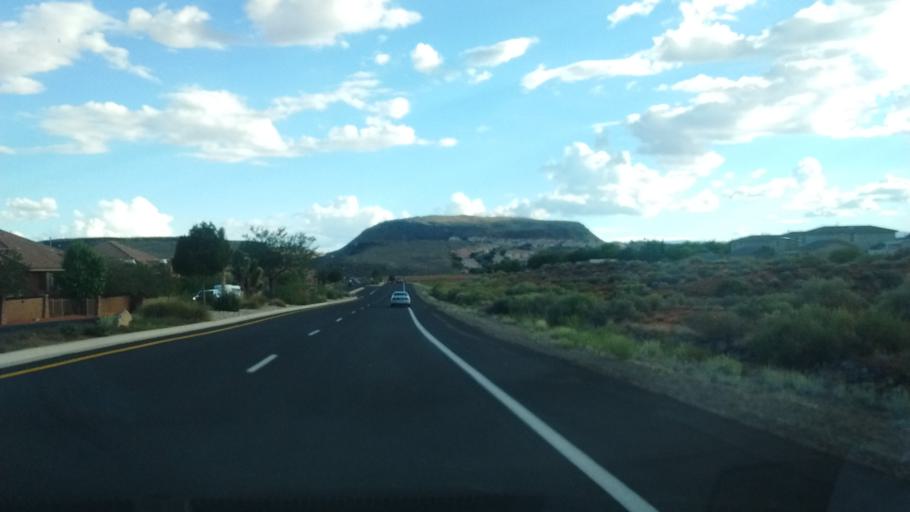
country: US
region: Utah
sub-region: Washington County
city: Washington
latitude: 37.1370
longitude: -113.4857
